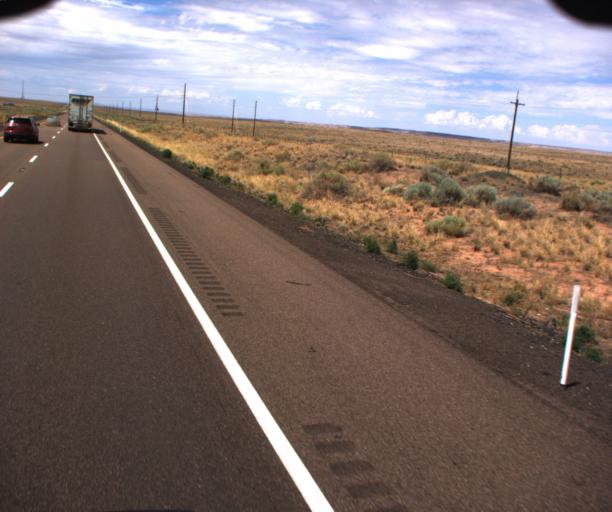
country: US
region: Arizona
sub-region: Navajo County
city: Holbrook
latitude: 35.0375
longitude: -109.8215
